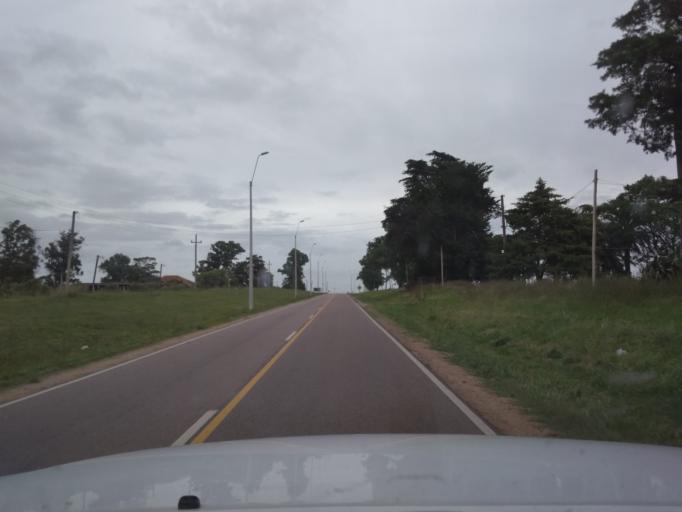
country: UY
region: Canelones
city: Tala
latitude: -34.3580
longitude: -55.7732
